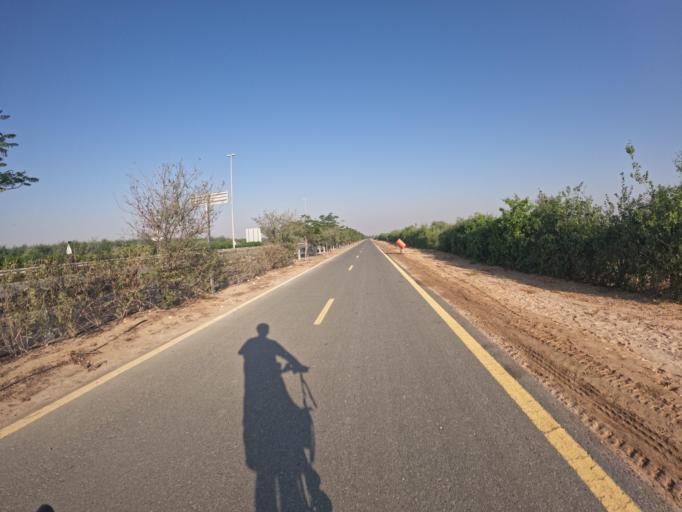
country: AE
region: Dubai
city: Dubai
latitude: 24.8536
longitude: 55.3441
